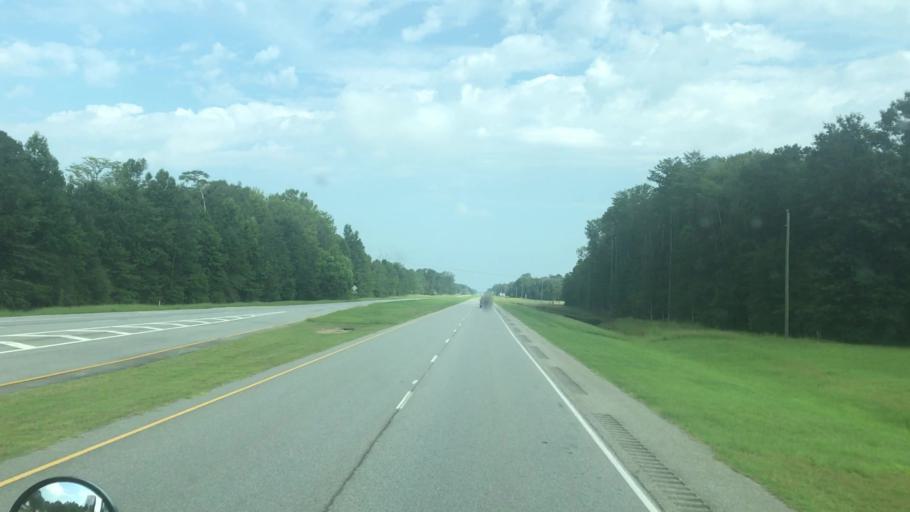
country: US
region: Georgia
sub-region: Early County
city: Blakely
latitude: 31.2808
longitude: -84.8377
